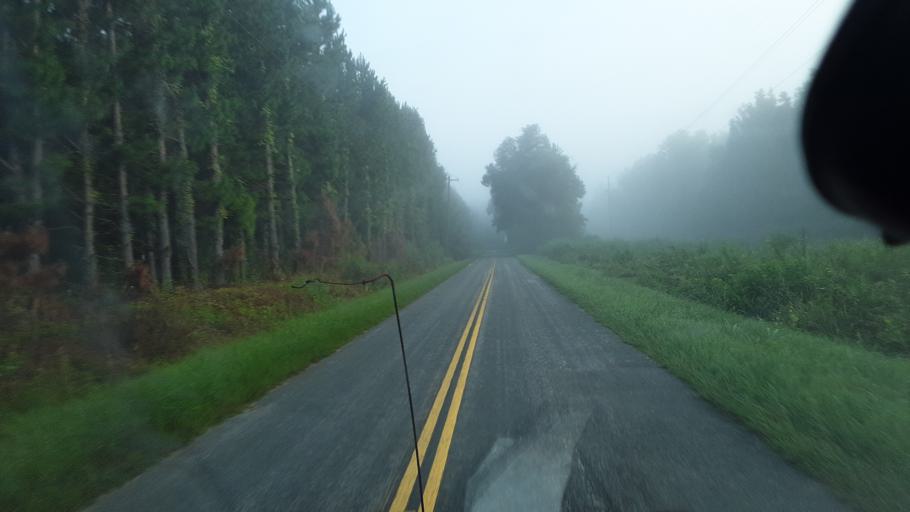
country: US
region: South Carolina
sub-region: Williamsburg County
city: Kingstree
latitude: 33.8137
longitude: -79.9625
